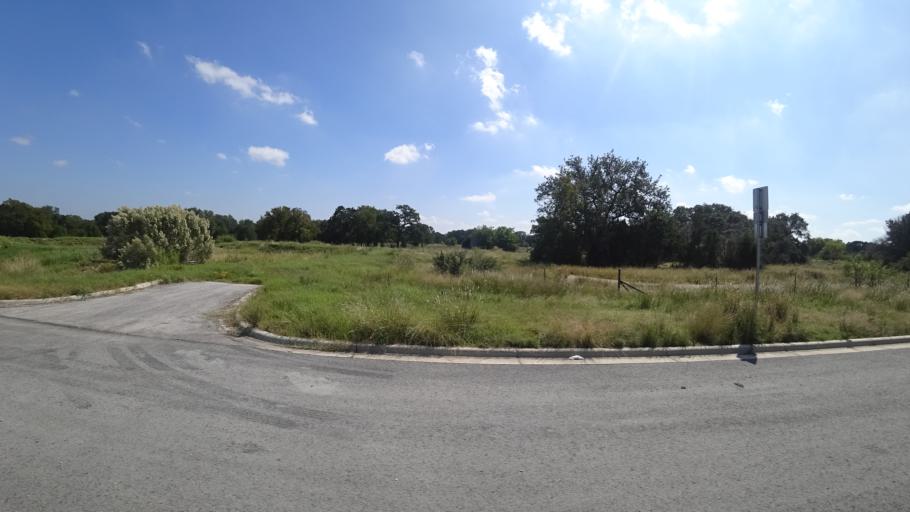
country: US
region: Texas
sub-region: Williamson County
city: Brushy Creek
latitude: 30.5082
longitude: -97.7146
